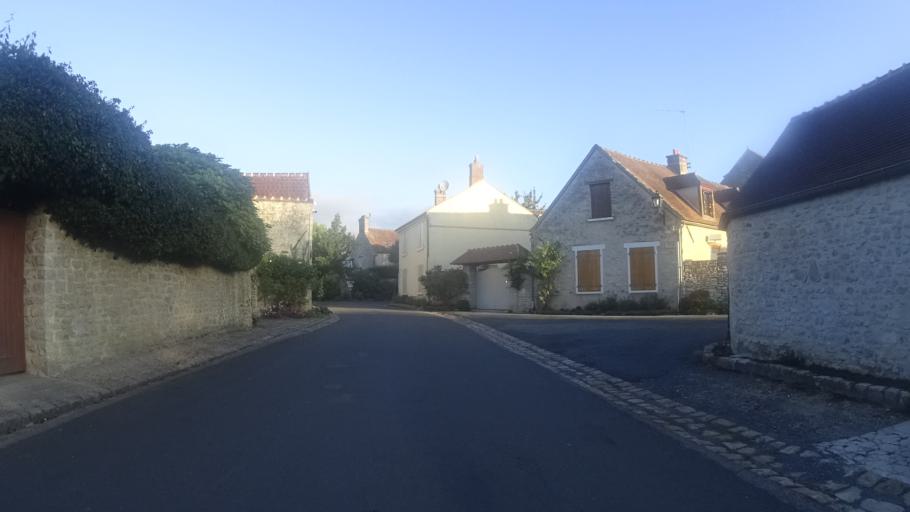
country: FR
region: Picardie
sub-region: Departement de l'Oise
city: Chamant
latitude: 49.1792
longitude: 2.6717
